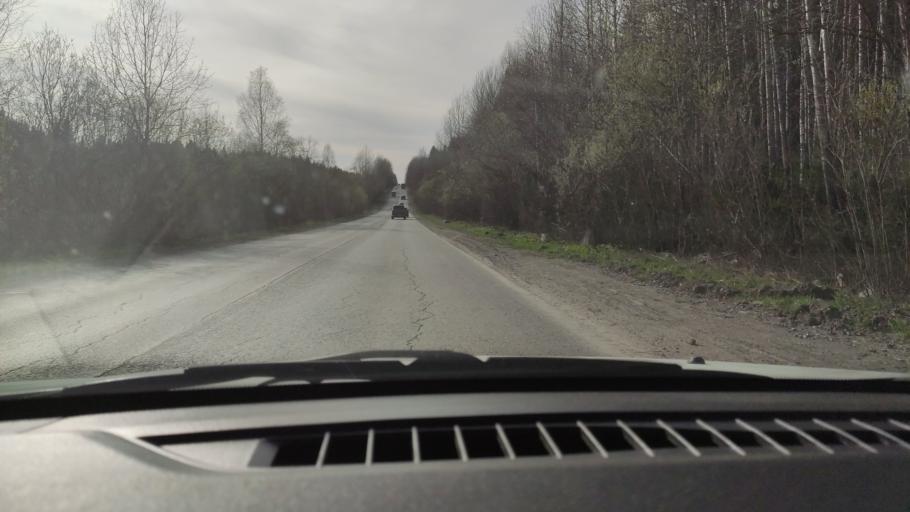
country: RU
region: Perm
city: Ferma
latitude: 57.9362
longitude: 56.4677
